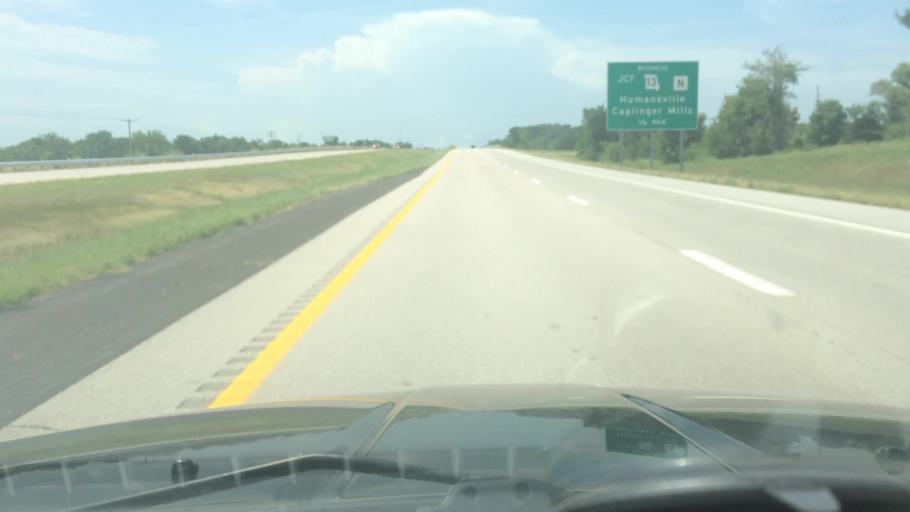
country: US
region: Missouri
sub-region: Polk County
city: Humansville
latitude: 37.7917
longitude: -93.5861
